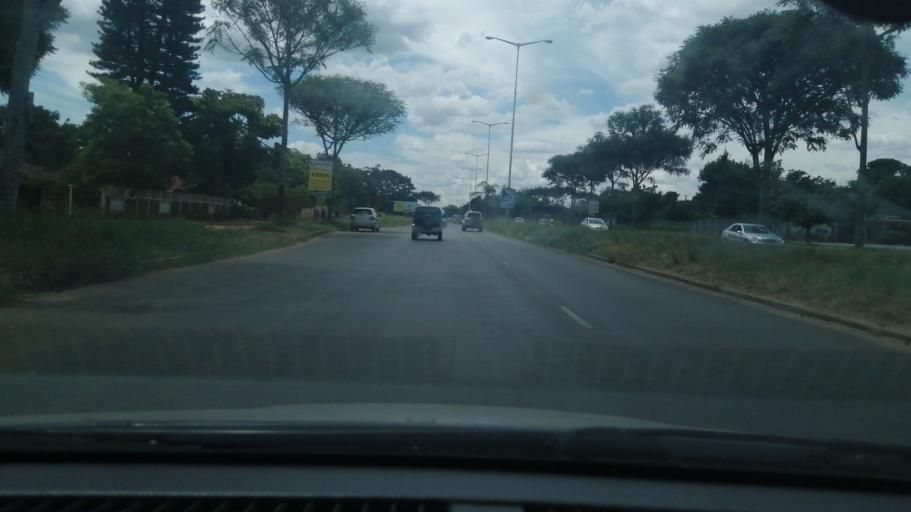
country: ZW
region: Harare
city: Harare
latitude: -17.8273
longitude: 31.0981
